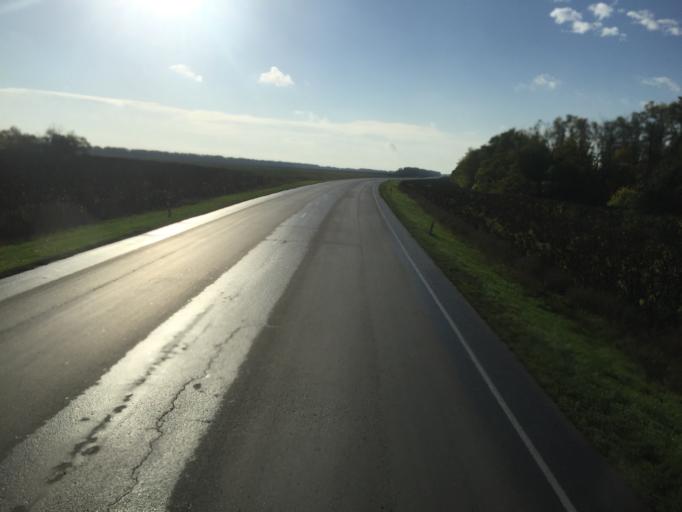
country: RU
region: Rostov
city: Yegorlykskaya
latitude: 46.6527
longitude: 40.5677
